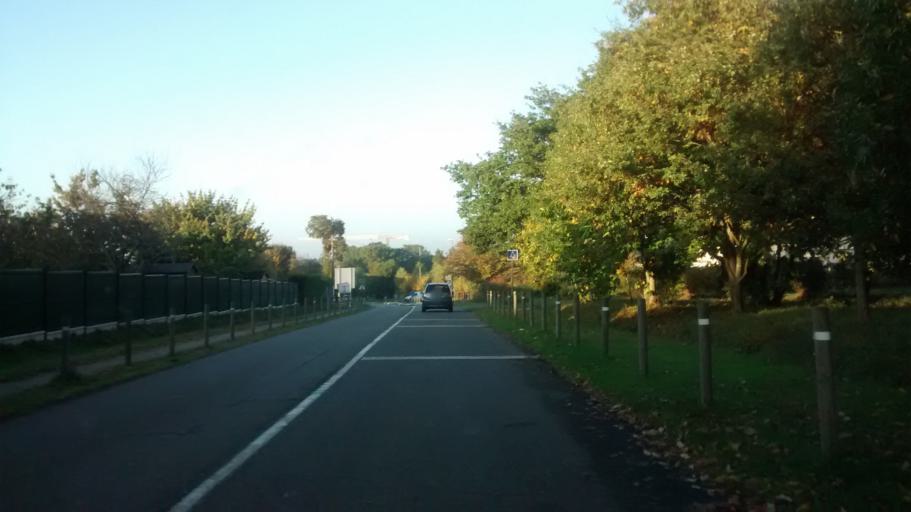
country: FR
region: Brittany
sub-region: Departement d'Ille-et-Vilaine
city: Le Rheu
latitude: 48.1234
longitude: -1.8053
